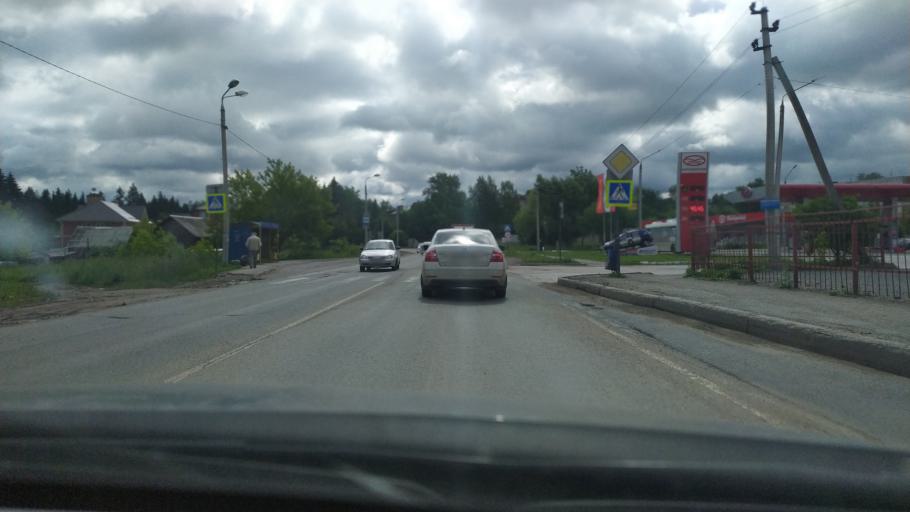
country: RU
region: Perm
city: Froly
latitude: 57.9767
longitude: 56.3146
